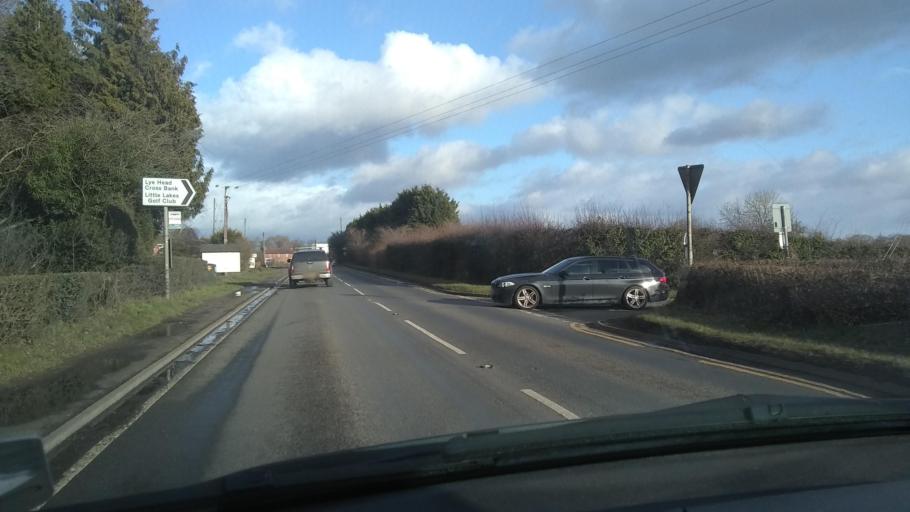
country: GB
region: England
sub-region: Worcestershire
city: Bewdley
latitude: 52.3637
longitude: -2.3642
